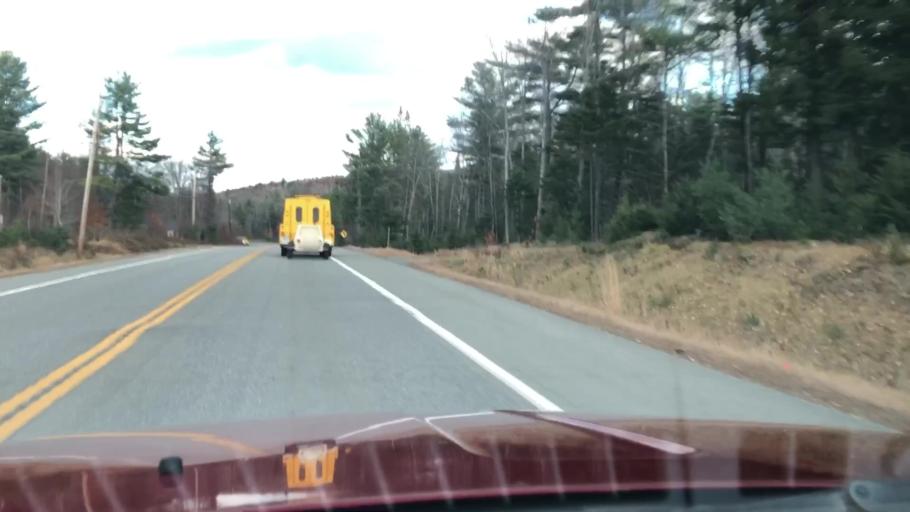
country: US
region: Maine
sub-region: Oxford County
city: Peru
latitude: 44.5469
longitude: -70.3957
